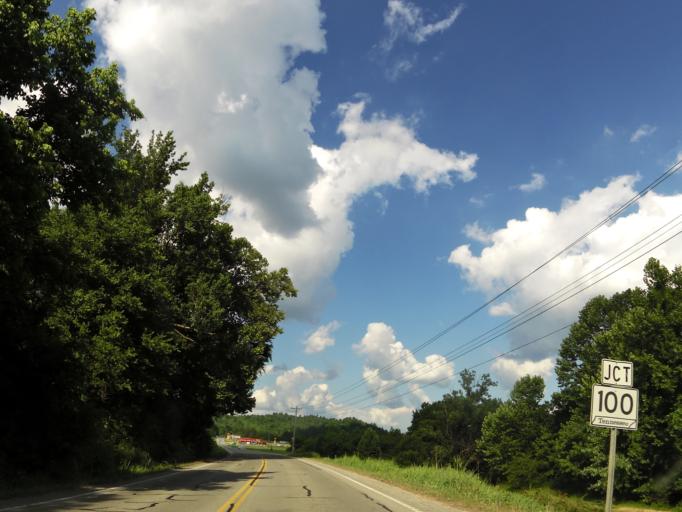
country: US
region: Tennessee
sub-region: Perry County
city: Linden
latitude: 35.6348
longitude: -87.7959
